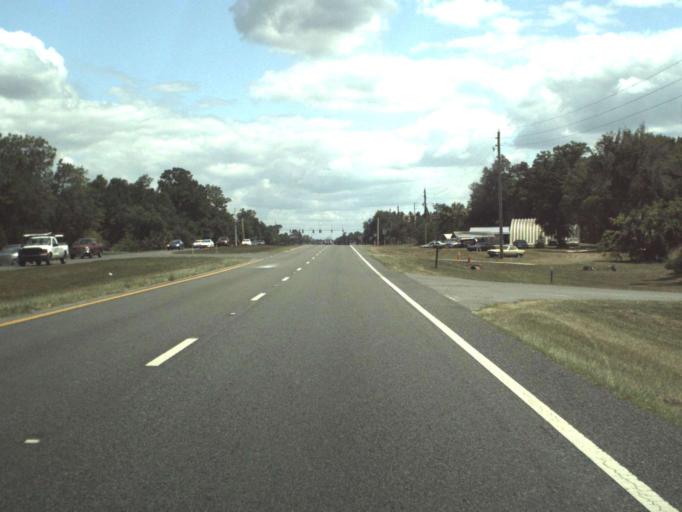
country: US
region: Florida
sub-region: Marion County
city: Ocala
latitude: 29.2265
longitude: -82.1486
